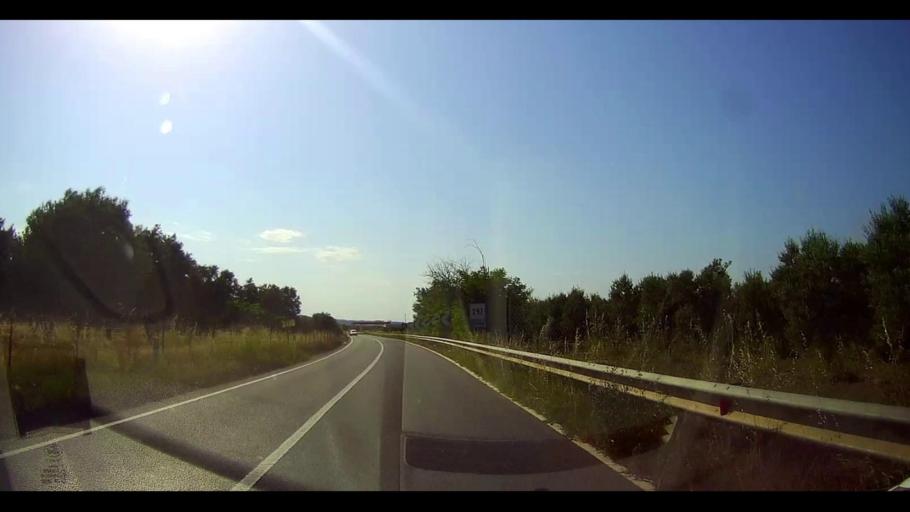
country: IT
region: Calabria
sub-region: Provincia di Crotone
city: Torretta
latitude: 39.4782
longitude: 16.9982
